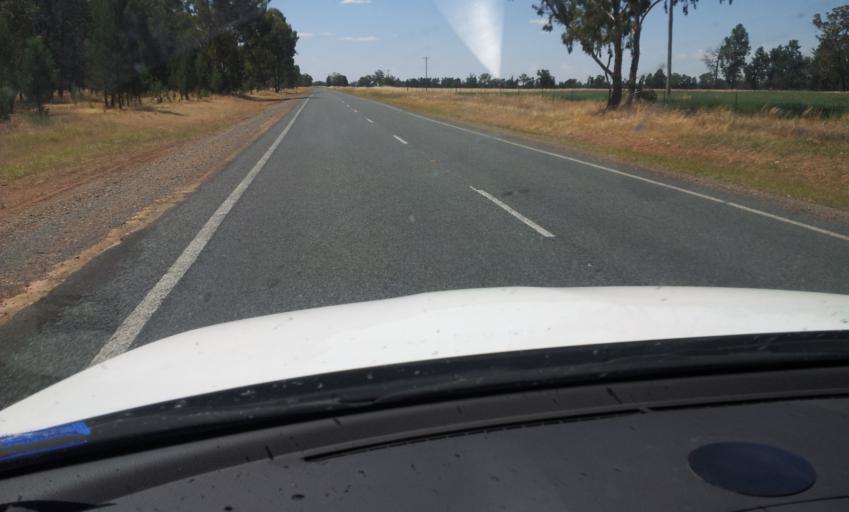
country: AU
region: New South Wales
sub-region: Corowa Shire
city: Corowa
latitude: -35.7114
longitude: 146.3366
